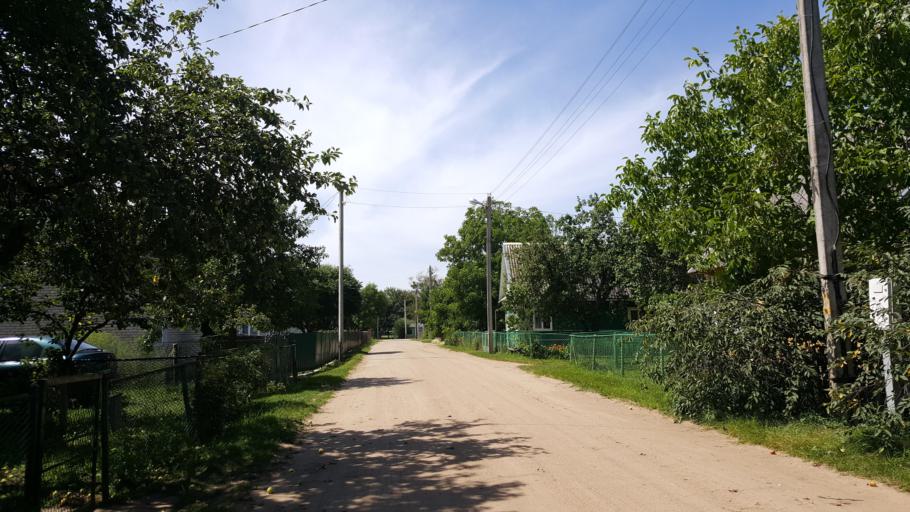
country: BY
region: Brest
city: Pruzhany
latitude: 52.5644
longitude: 24.2179
